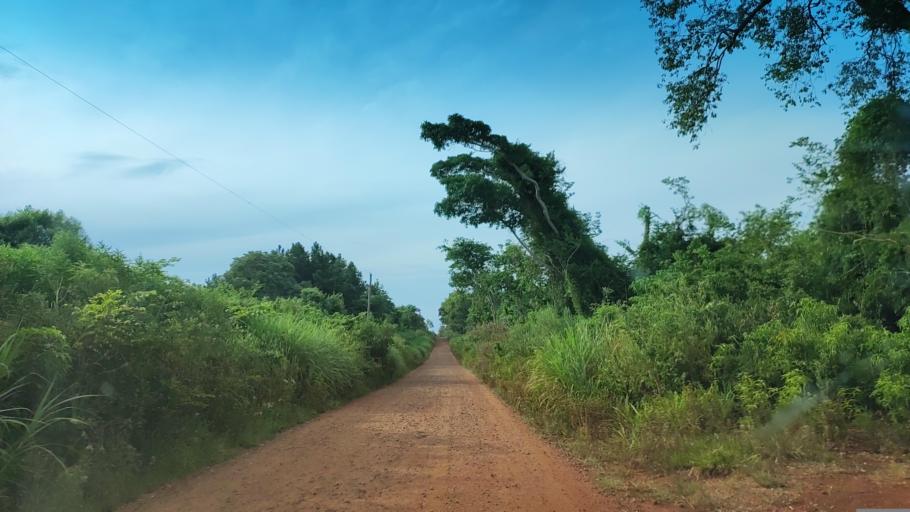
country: AR
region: Misiones
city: Gobernador Roca
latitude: -27.1572
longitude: -55.5238
